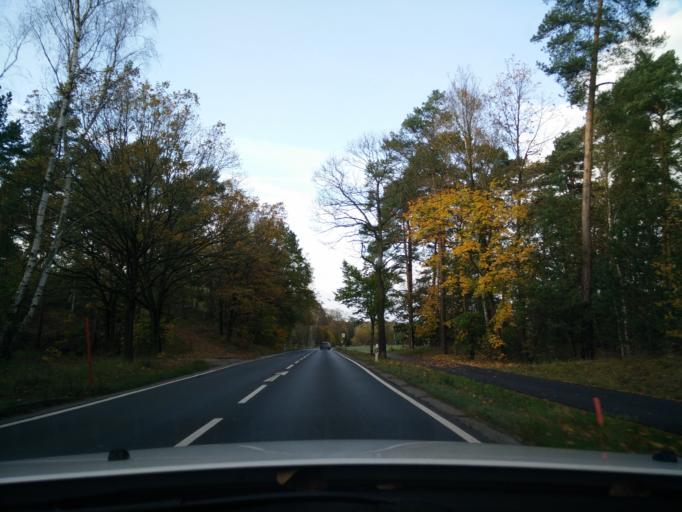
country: DE
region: Brandenburg
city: Falkensee
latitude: 52.5855
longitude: 13.0994
